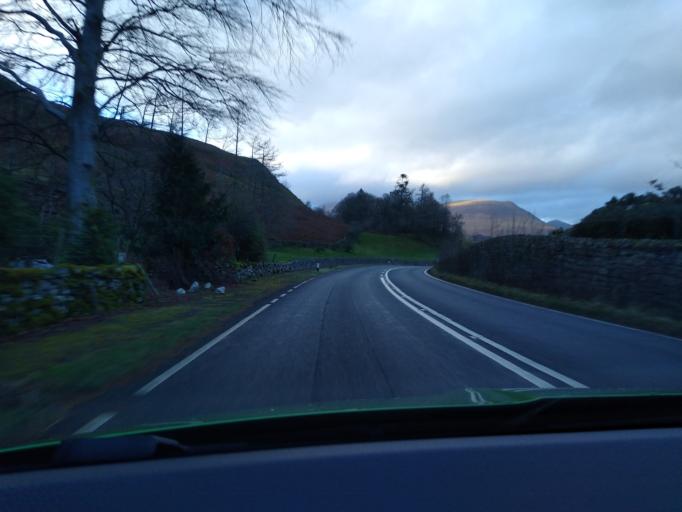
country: GB
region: England
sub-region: Cumbria
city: Keswick
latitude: 54.5798
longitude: -3.0867
